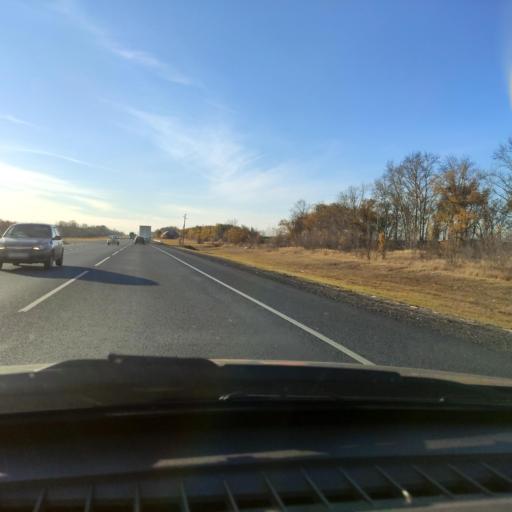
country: RU
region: Samara
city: Varlamovo
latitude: 53.1952
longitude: 48.2750
